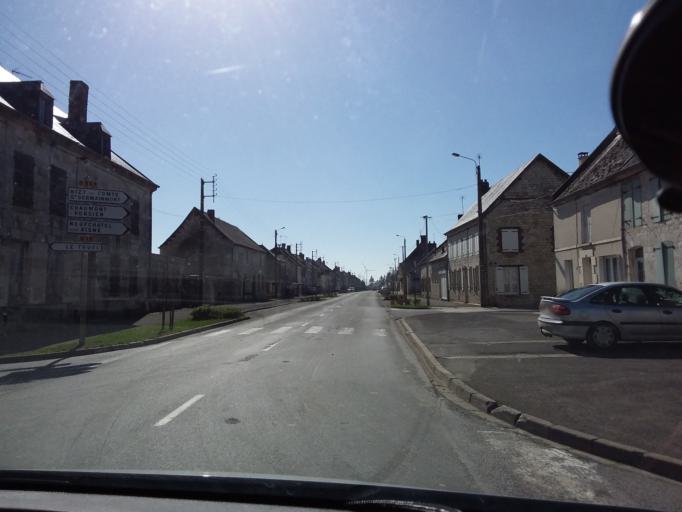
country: FR
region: Picardie
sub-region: Departement de l'Aisne
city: Montcornet
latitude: 49.6298
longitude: 4.0222
